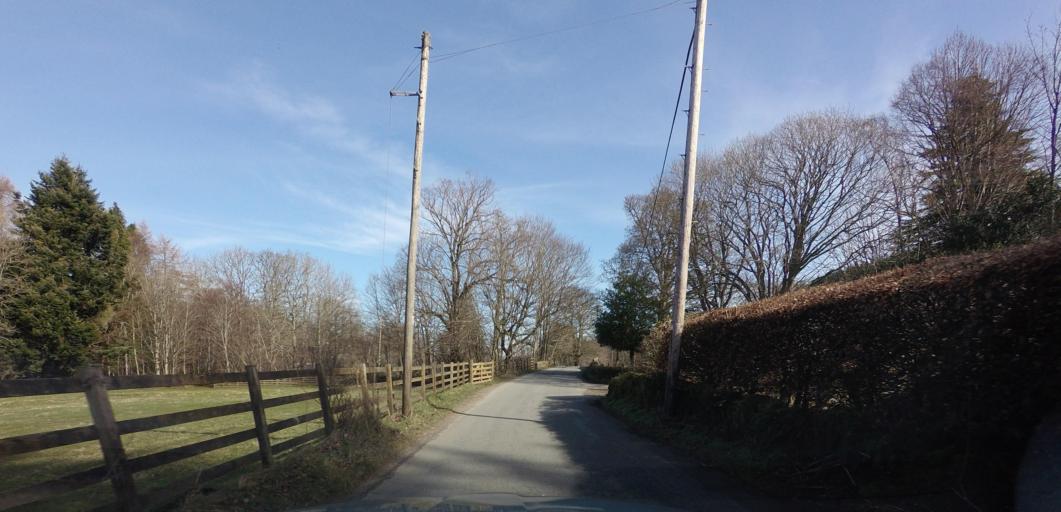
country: GB
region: Scotland
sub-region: Perth and Kinross
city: Aberfeldy
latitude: 56.5722
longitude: -4.0194
